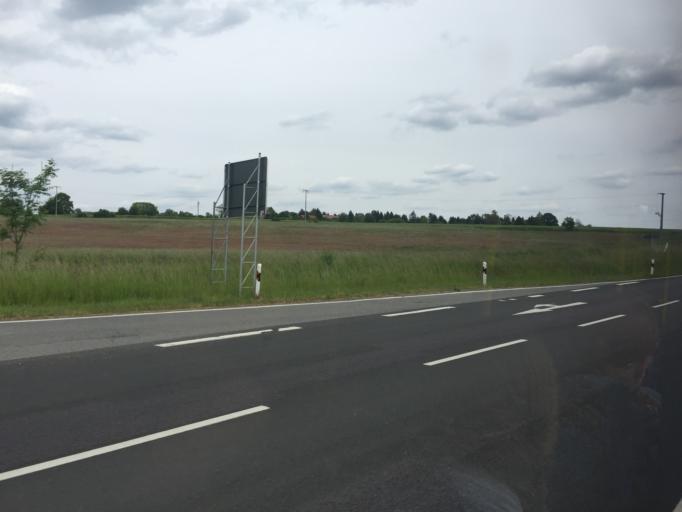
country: DE
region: Saxony
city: Reichenbach
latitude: 51.1485
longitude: 14.8071
